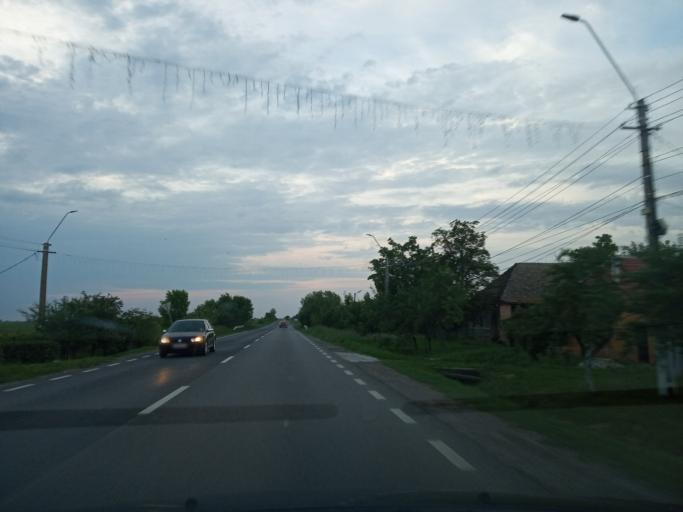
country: RO
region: Timis
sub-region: Comuna Voiteg
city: Voiteg
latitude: 45.4736
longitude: 21.2342
